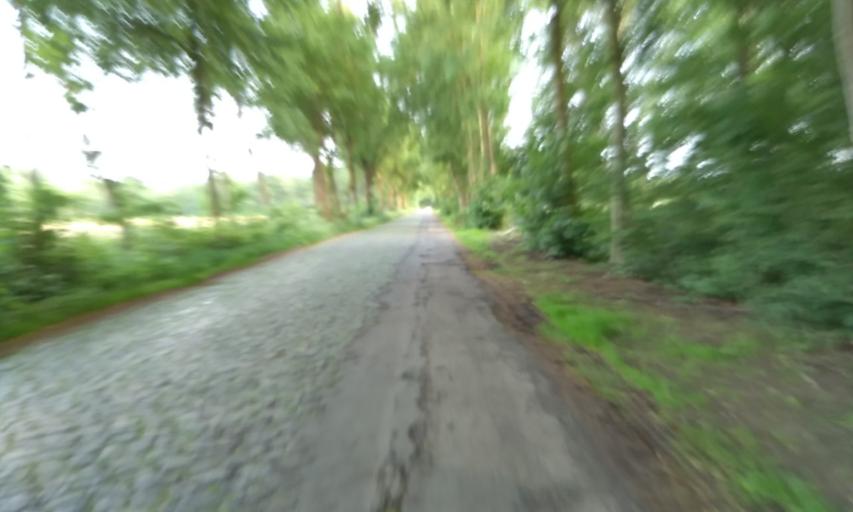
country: DE
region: Lower Saxony
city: Deinste
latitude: 53.5111
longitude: 9.4494
